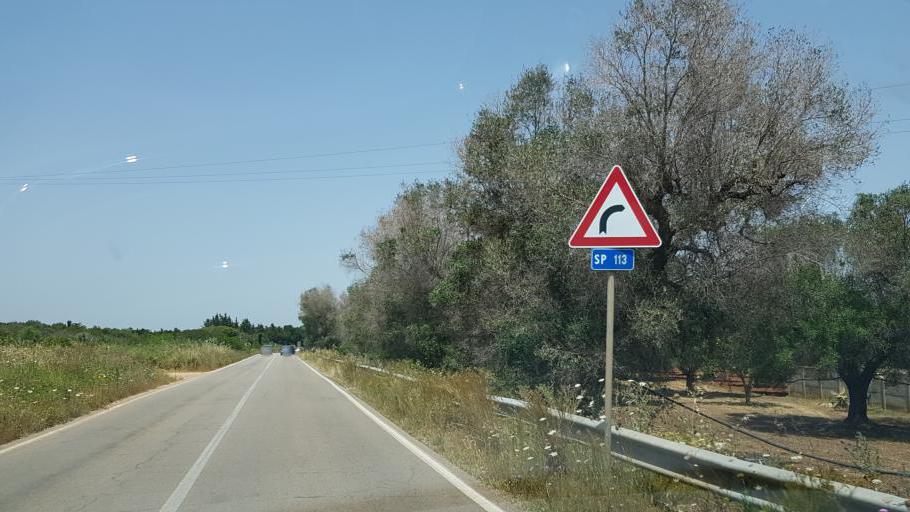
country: IT
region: Apulia
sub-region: Provincia di Lecce
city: Porto Cesareo
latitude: 40.3001
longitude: 17.9185
